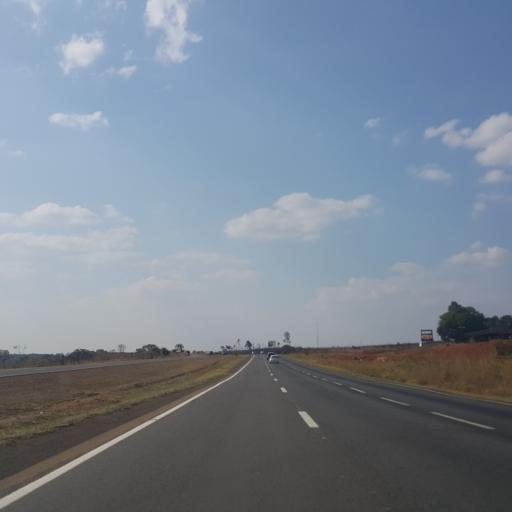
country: BR
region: Goias
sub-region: Abadiania
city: Abadiania
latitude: -16.2529
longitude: -48.7624
